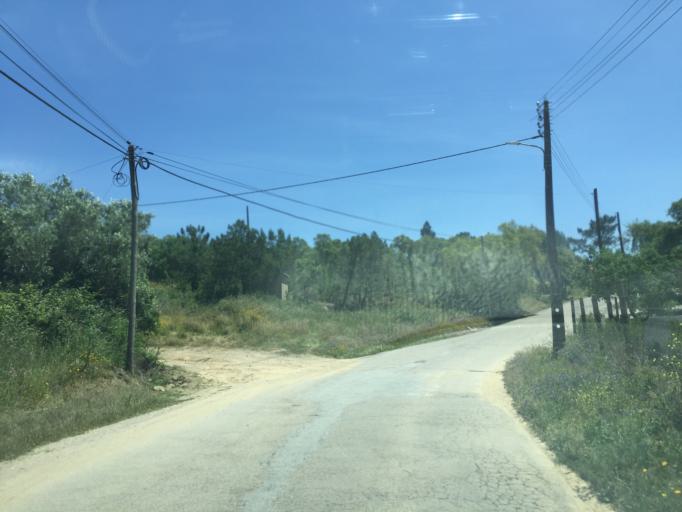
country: PT
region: Lisbon
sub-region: Mafra
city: Venda do Pinheiro
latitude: 38.8959
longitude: -9.2301
